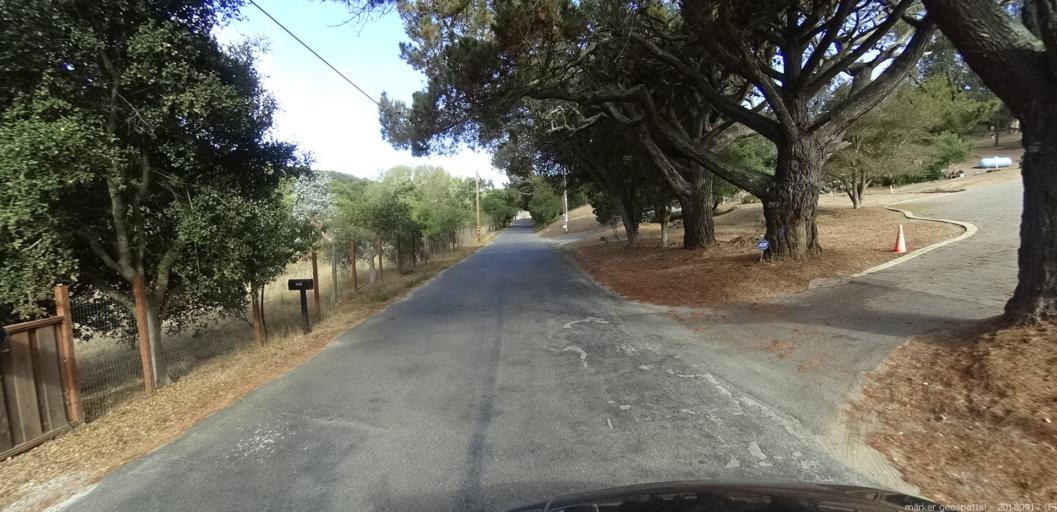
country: US
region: California
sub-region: Monterey County
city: Elkhorn
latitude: 36.8052
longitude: -121.7078
